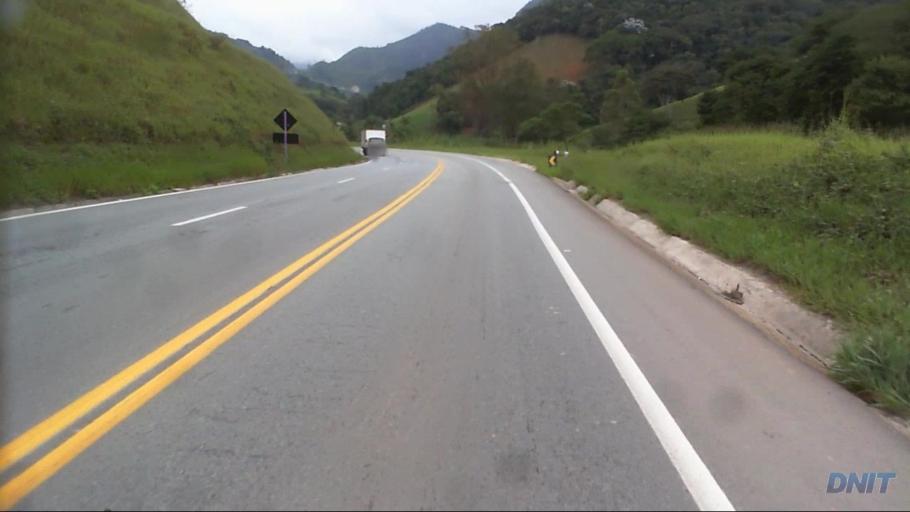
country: BR
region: Minas Gerais
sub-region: Nova Era
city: Nova Era
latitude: -19.6426
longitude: -42.9199
